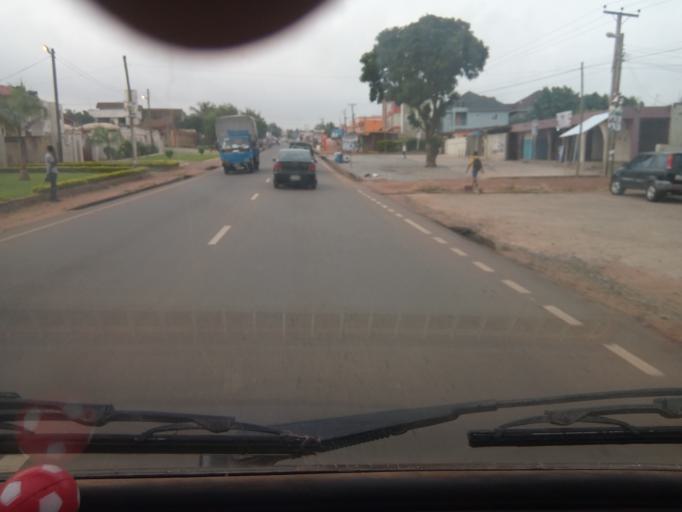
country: GH
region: Greater Accra
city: Medina Estates
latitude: 5.6779
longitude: -0.1911
